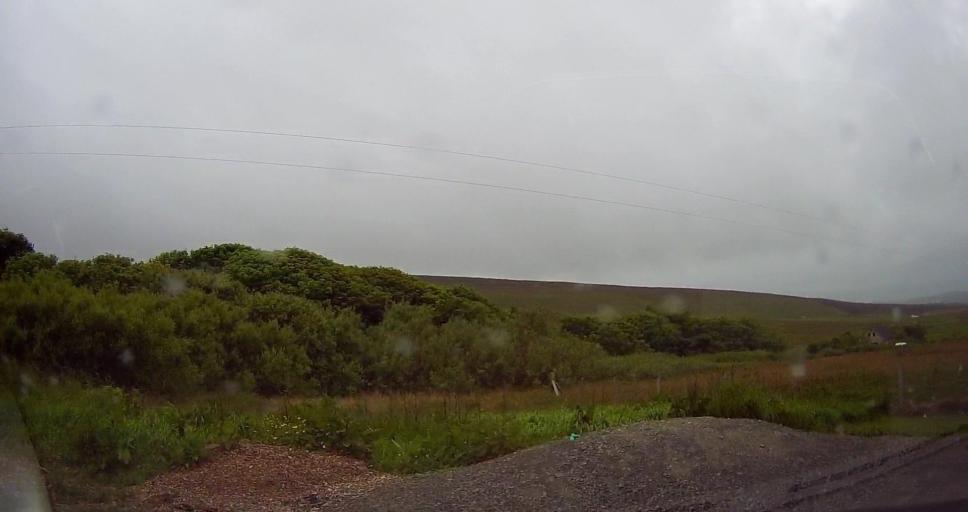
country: GB
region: Scotland
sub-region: Orkney Islands
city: Stromness
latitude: 58.9775
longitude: -3.1723
